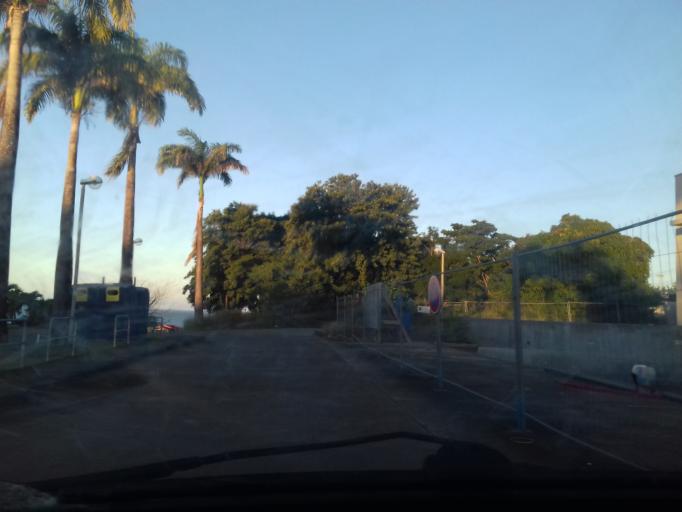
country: MQ
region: Martinique
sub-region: Martinique
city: Fort-de-France
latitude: 14.6204
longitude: -61.0942
